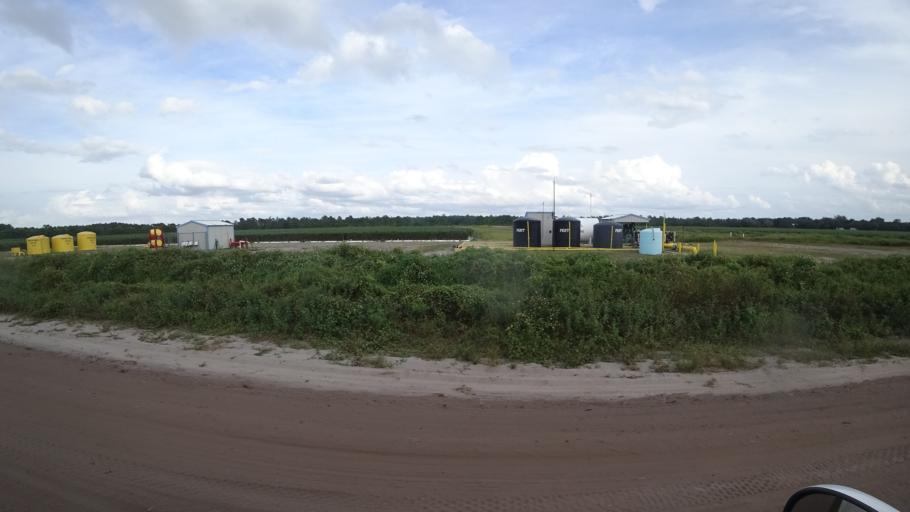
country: US
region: Florida
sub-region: Hillsborough County
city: Wimauma
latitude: 27.6152
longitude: -82.1333
